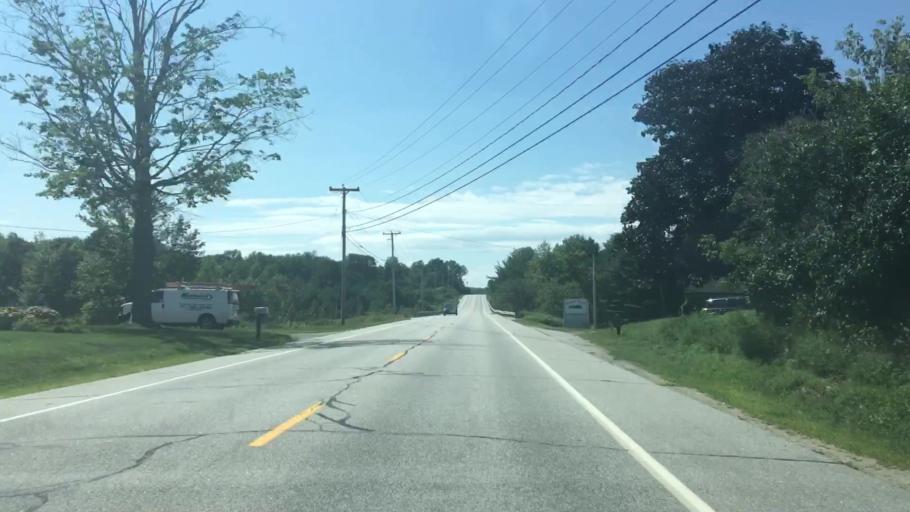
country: US
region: Maine
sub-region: Kennebec County
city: Monmouth
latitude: 44.1697
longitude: -70.0133
